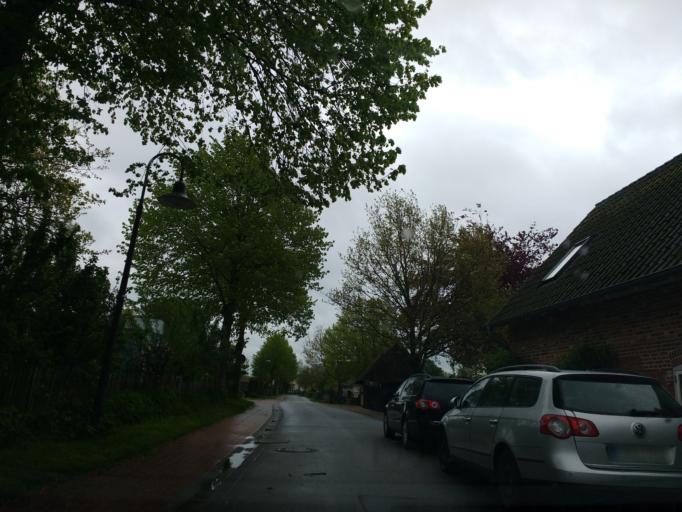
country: DE
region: Schleswig-Holstein
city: Waabs
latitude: 54.5167
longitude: 9.9790
